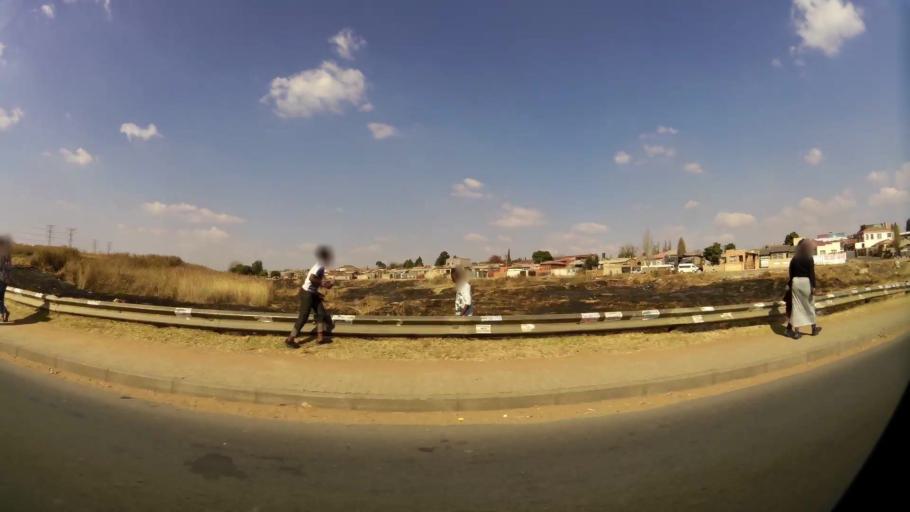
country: ZA
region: Gauteng
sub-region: City of Johannesburg Metropolitan Municipality
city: Soweto
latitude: -26.2548
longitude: 27.9442
